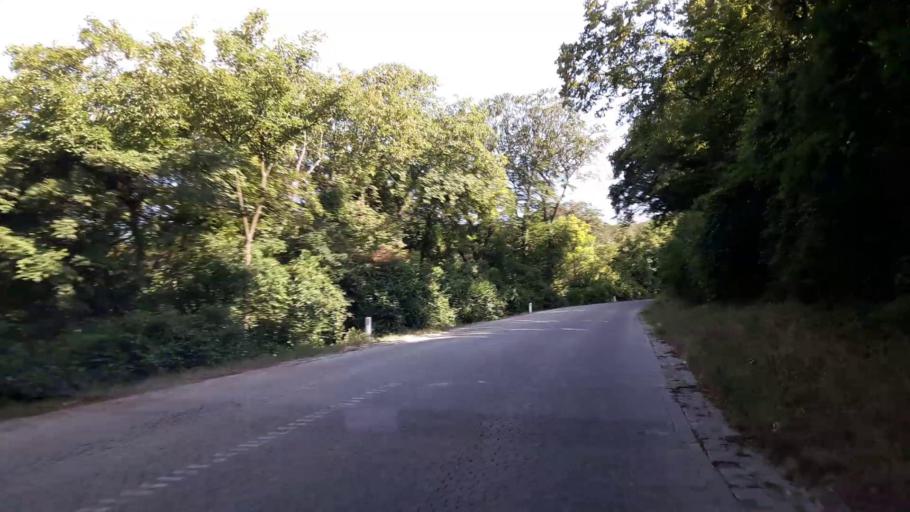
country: AT
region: Lower Austria
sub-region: Politischer Bezirk Wien-Umgebung
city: Klosterneuburg
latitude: 48.2832
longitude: 16.3254
